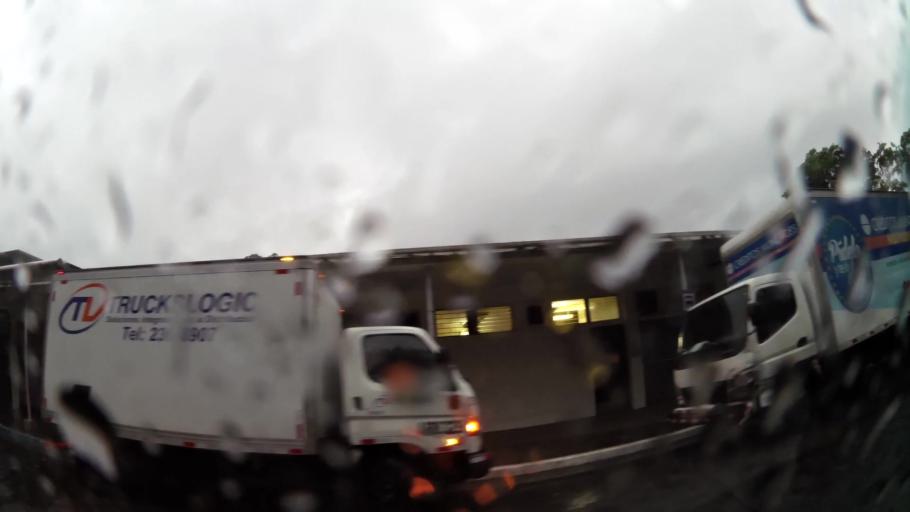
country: PA
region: Panama
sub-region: Distrito de Panama
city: Paraiso
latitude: 9.0278
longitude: -79.6252
